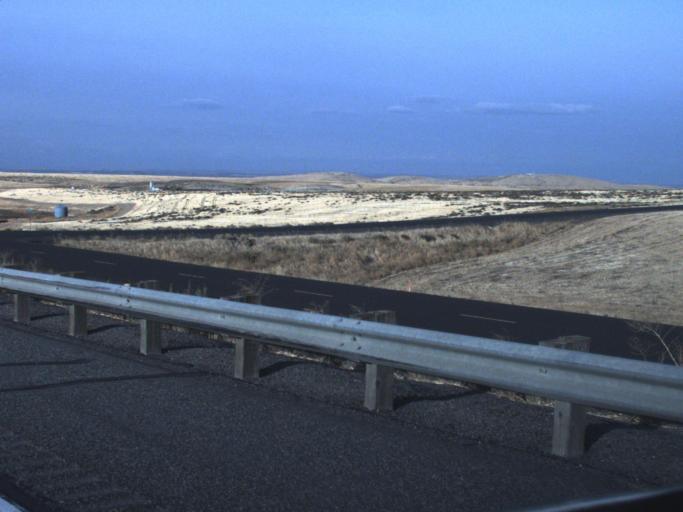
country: US
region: Washington
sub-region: Benton County
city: Highland
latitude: 46.1342
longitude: -119.2019
